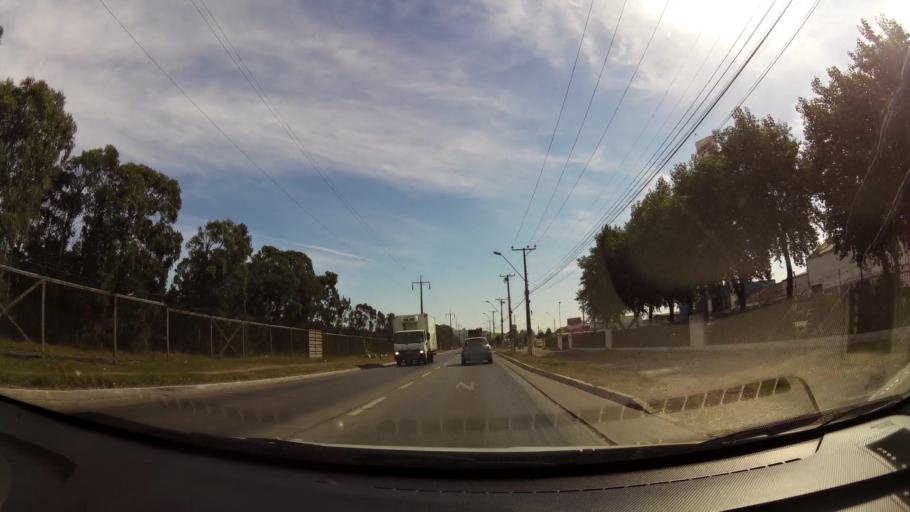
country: CL
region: Biobio
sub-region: Provincia de Concepcion
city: Talcahuano
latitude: -36.7349
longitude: -73.1198
